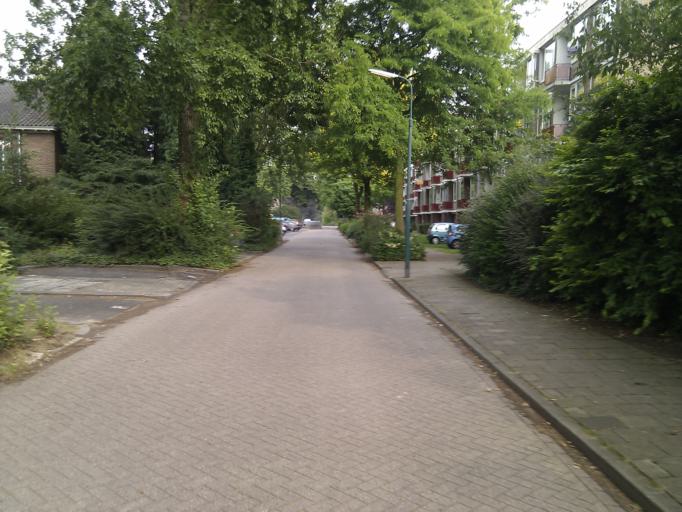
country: NL
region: Utrecht
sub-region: Gemeente De Bilt
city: De Bilt
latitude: 52.1112
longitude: 5.1861
